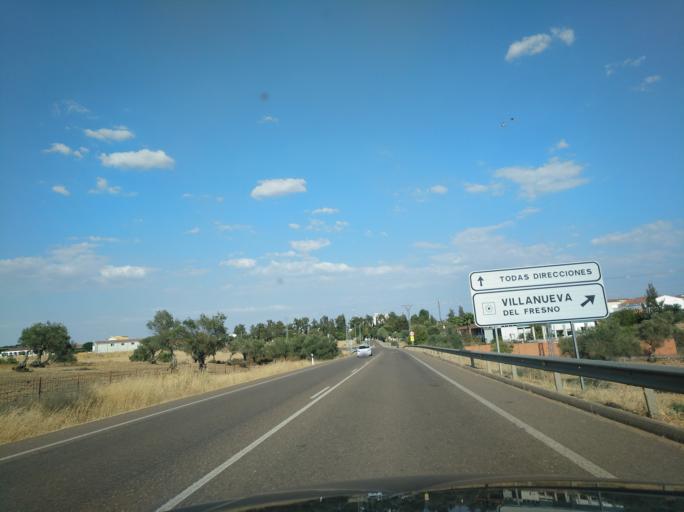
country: ES
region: Extremadura
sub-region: Provincia de Badajoz
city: Villanueva del Fresno
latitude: 38.3777
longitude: -7.1713
